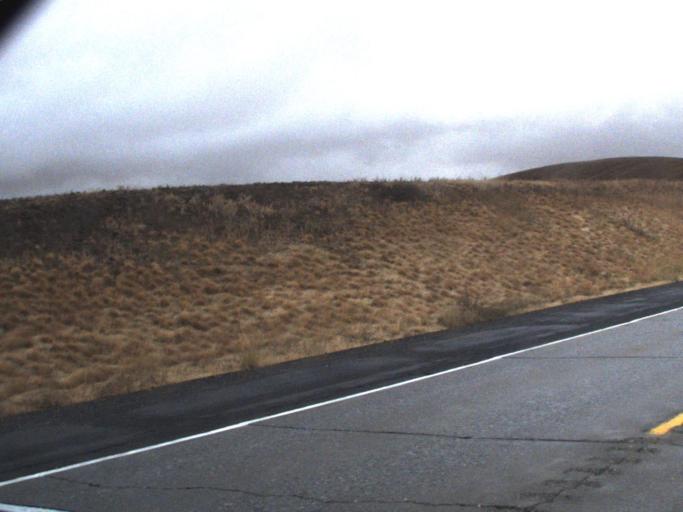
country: US
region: Washington
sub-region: Whitman County
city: Colfax
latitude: 47.1602
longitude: -117.3785
